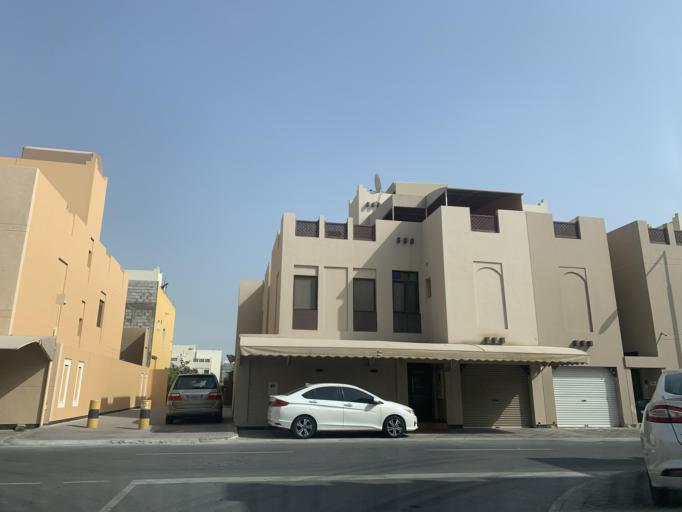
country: BH
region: Northern
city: Madinat `Isa
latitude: 26.1855
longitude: 50.5623
